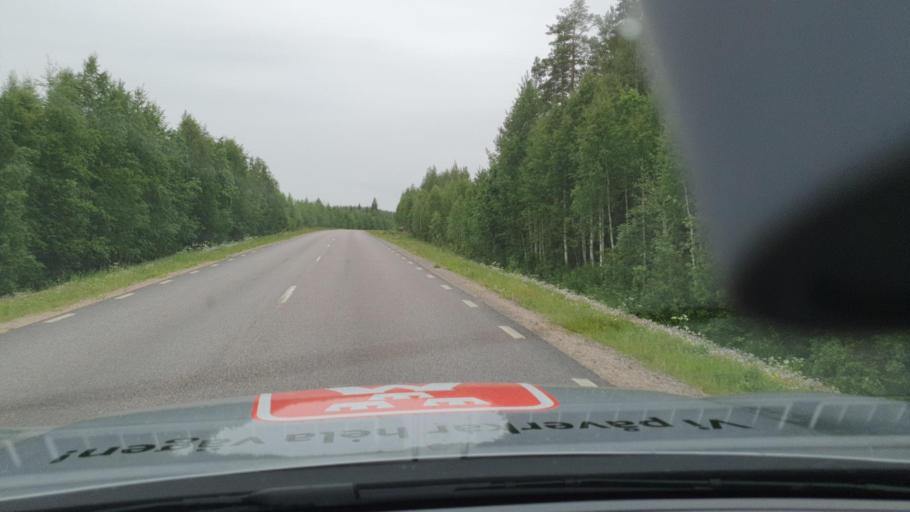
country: SE
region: Norrbotten
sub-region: Overtornea Kommun
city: OEvertornea
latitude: 66.4026
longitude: 23.4901
